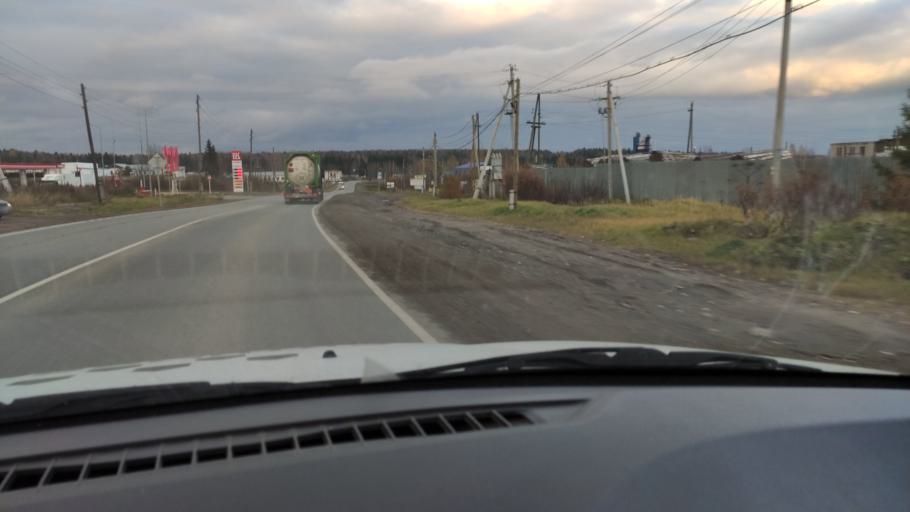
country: RU
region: Kirov
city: Omutninsk
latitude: 58.6941
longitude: 52.2184
